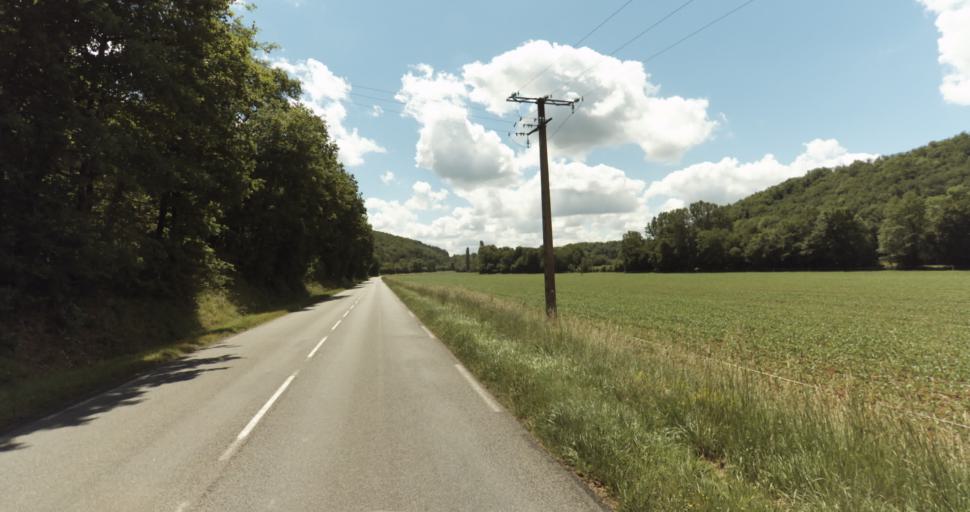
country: FR
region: Aquitaine
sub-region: Departement de la Dordogne
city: Beaumont-du-Perigord
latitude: 44.7941
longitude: 0.7551
